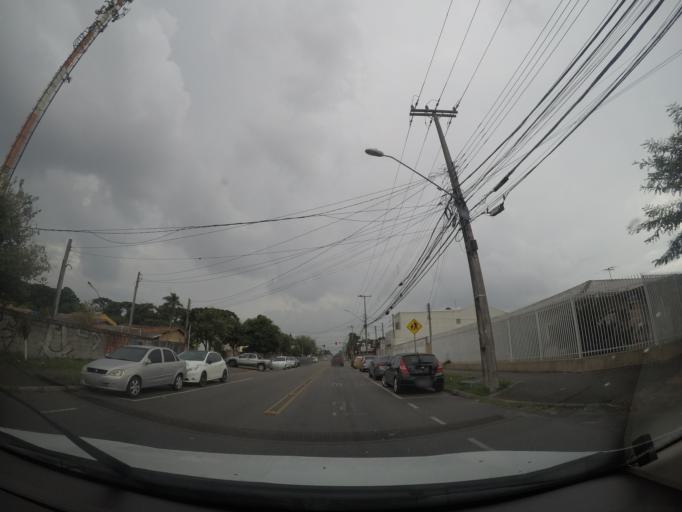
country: BR
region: Parana
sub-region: Sao Jose Dos Pinhais
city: Sao Jose dos Pinhais
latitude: -25.5150
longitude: -49.2448
